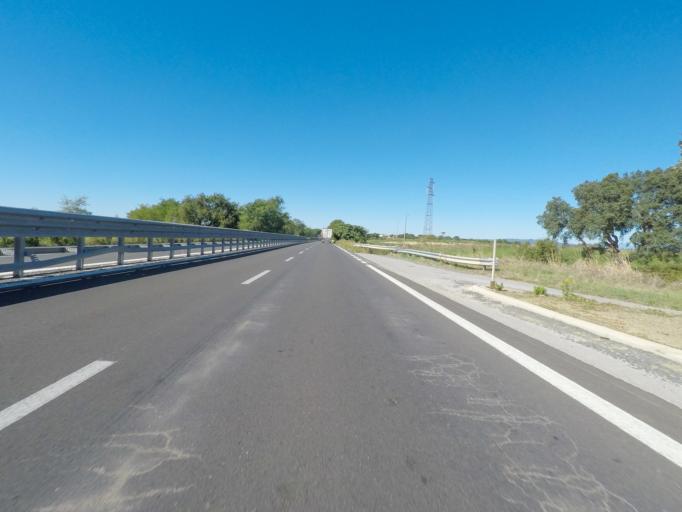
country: IT
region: Latium
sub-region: Provincia di Viterbo
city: Montalto di Castro
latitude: 42.3334
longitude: 11.6260
